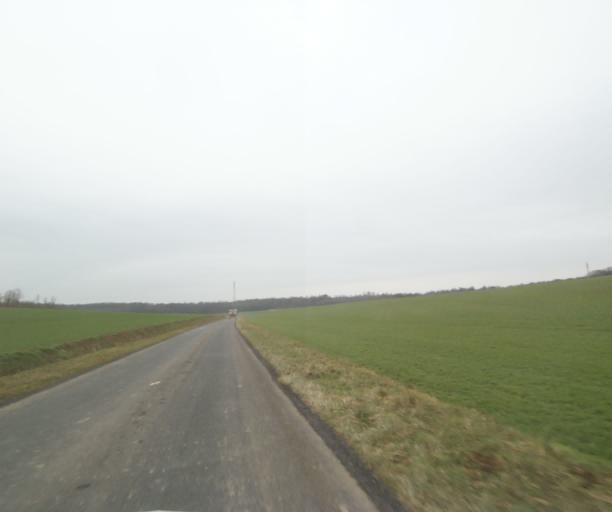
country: FR
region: Champagne-Ardenne
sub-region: Departement de la Haute-Marne
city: Bienville
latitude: 48.5780
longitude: 5.0314
